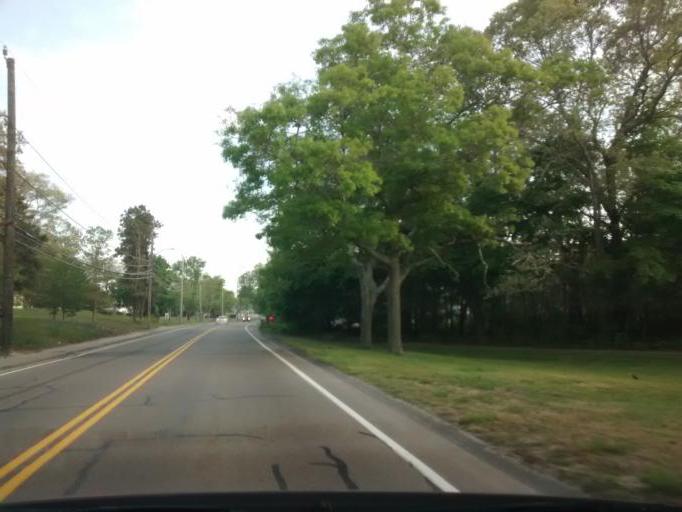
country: US
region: Massachusetts
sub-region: Barnstable County
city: Teaticket
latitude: 41.5707
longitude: -70.5944
